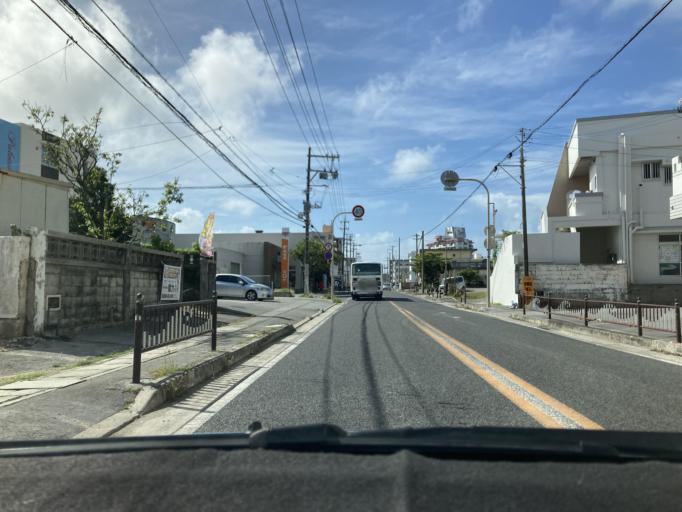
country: JP
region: Okinawa
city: Itoman
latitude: 26.1230
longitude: 127.6699
